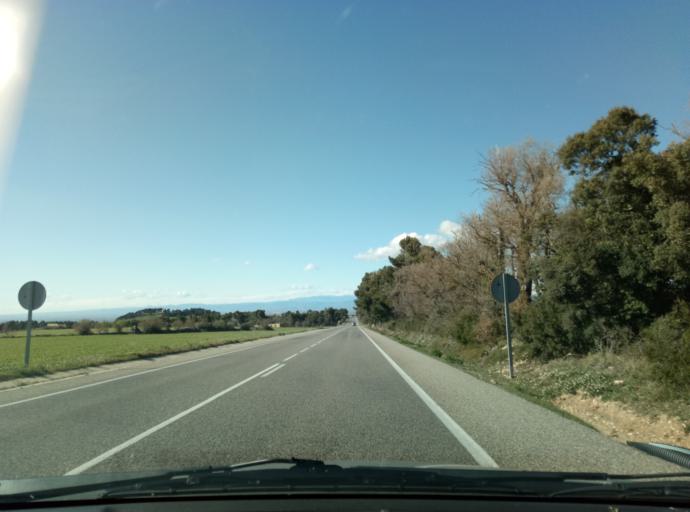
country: ES
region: Catalonia
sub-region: Provincia de Lleida
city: Ciutadilla
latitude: 41.5328
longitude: 1.1532
